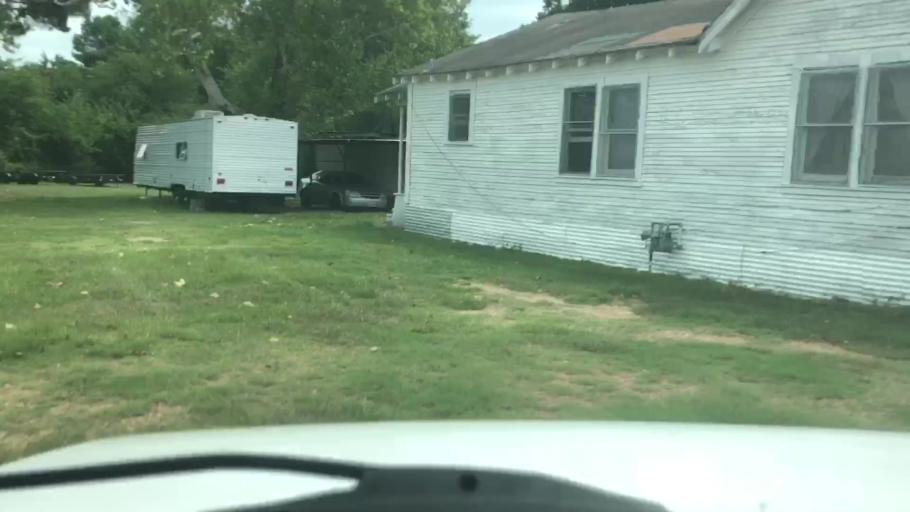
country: US
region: Texas
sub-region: Bowie County
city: Wake Village
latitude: 33.4422
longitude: -94.0896
